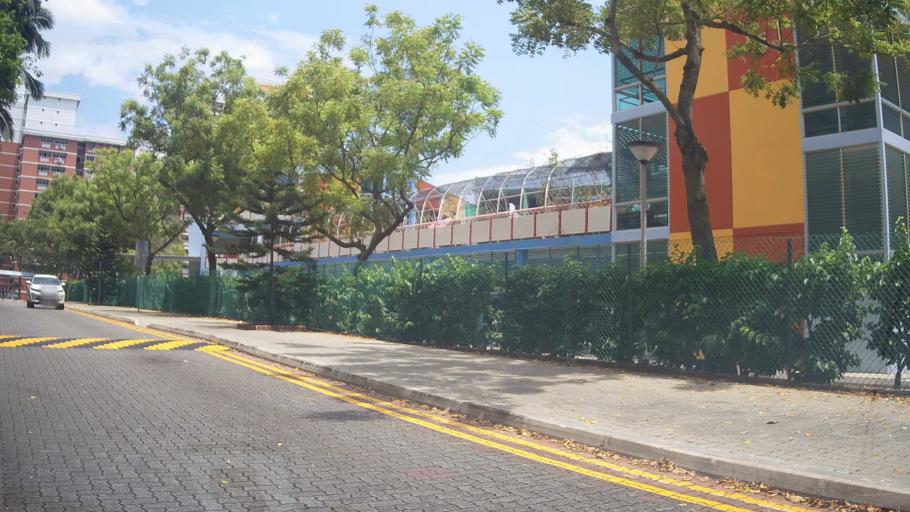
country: MY
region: Johor
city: Kampung Pasir Gudang Baru
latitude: 1.3760
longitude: 103.9345
